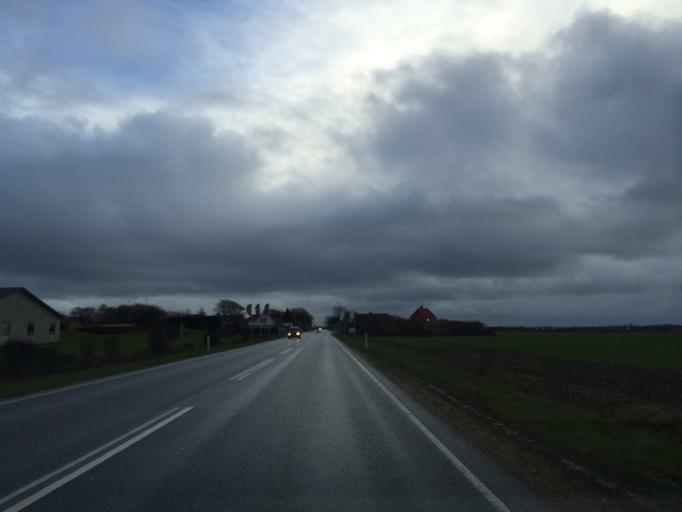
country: DK
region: Central Jutland
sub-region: Ringkobing-Skjern Kommune
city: Skjern
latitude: 56.0554
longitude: 8.3925
